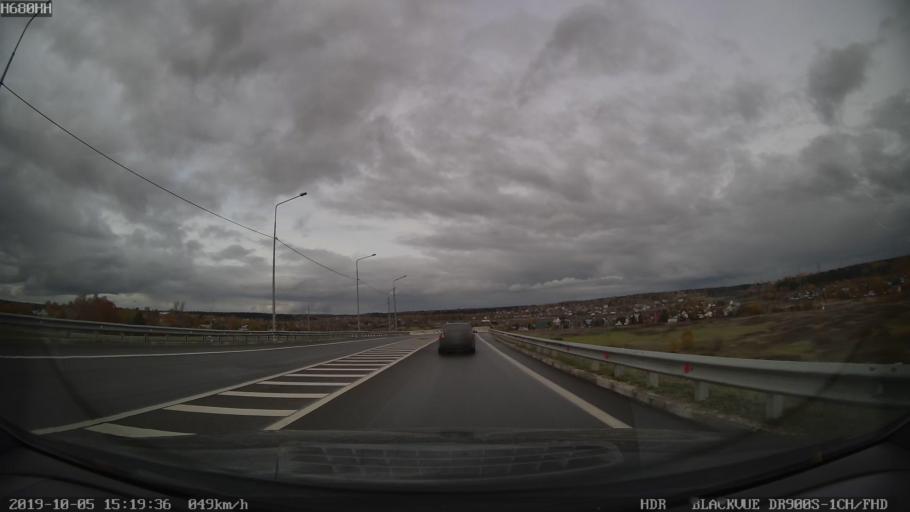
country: RU
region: Moskovskaya
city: Solnechnogorsk
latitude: 56.2202
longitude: 36.9068
